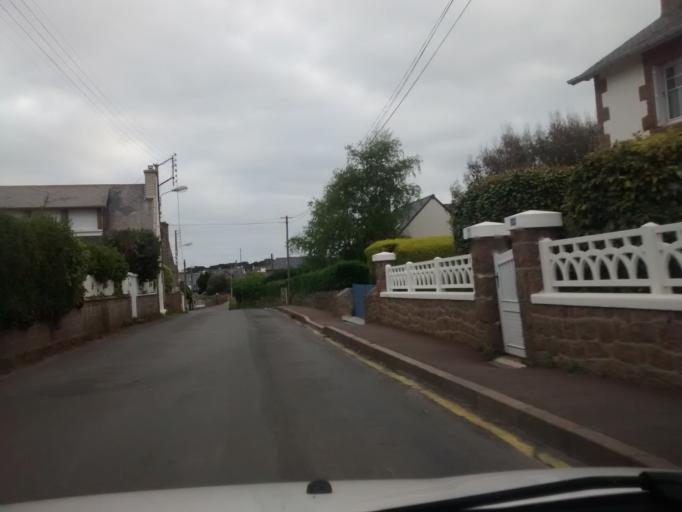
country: FR
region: Brittany
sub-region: Departement des Cotes-d'Armor
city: Tregastel
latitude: 48.8280
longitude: -3.4835
